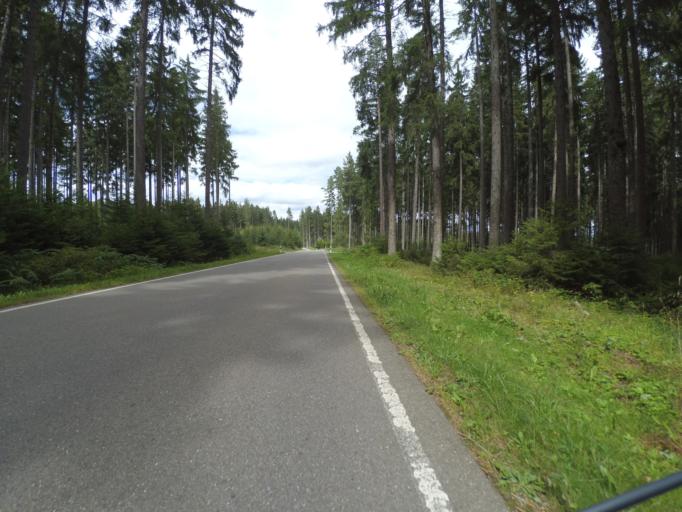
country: DE
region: Baden-Wuerttemberg
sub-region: Freiburg Region
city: Loffingen
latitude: 47.9412
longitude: 8.3624
